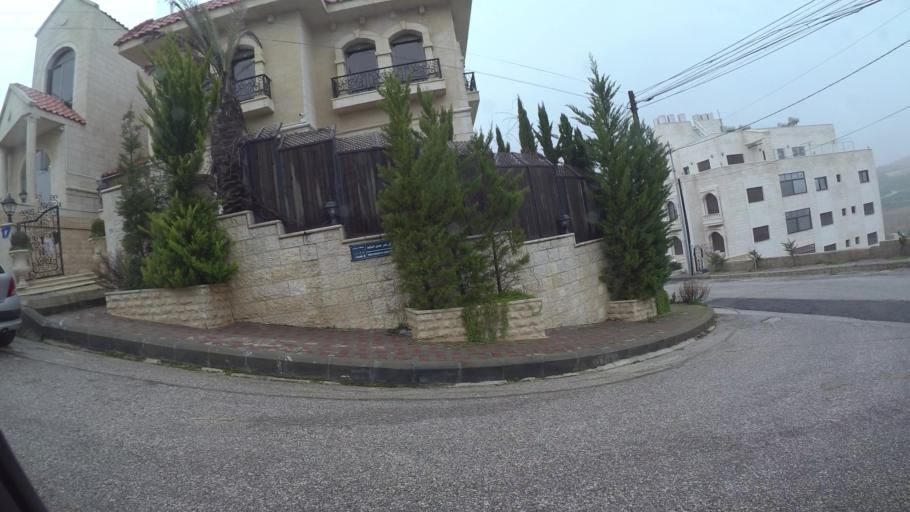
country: JO
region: Amman
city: Wadi as Sir
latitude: 31.9996
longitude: 35.8191
